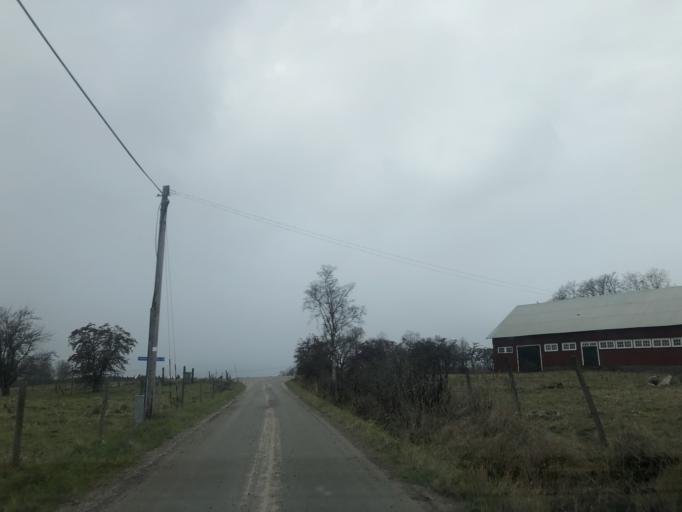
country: SE
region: Vaestra Goetaland
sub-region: Tranemo Kommun
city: Limmared
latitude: 57.6531
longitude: 13.3518
